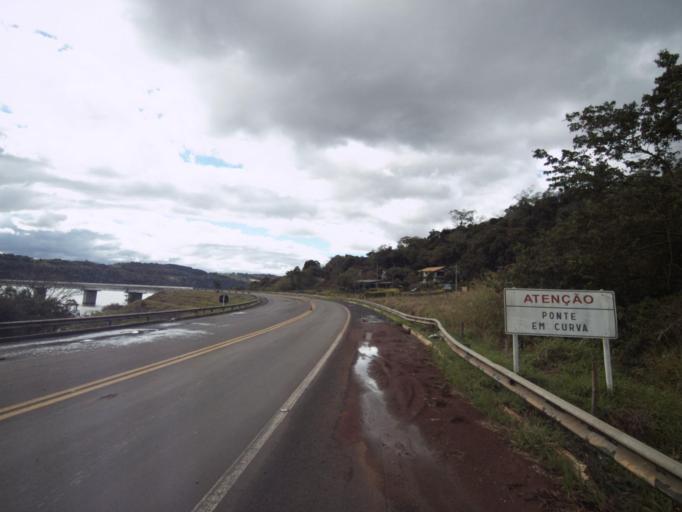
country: BR
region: Santa Catarina
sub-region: Concordia
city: Concordia
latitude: -27.3806
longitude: -51.9867
